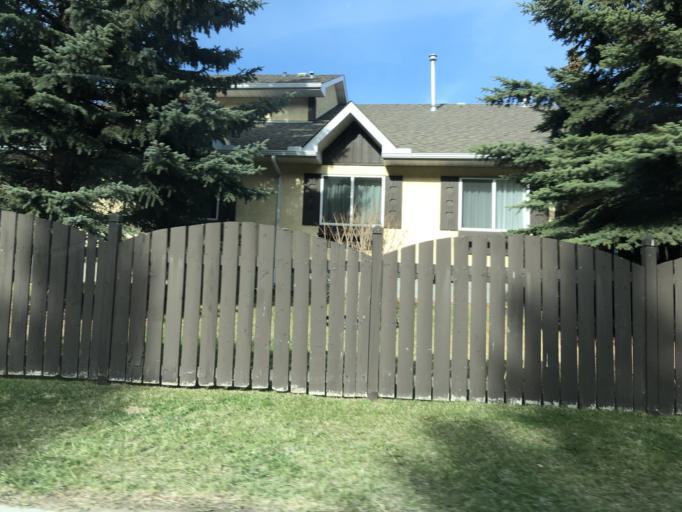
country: CA
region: Alberta
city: Canmore
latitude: 51.0820
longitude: -115.3681
